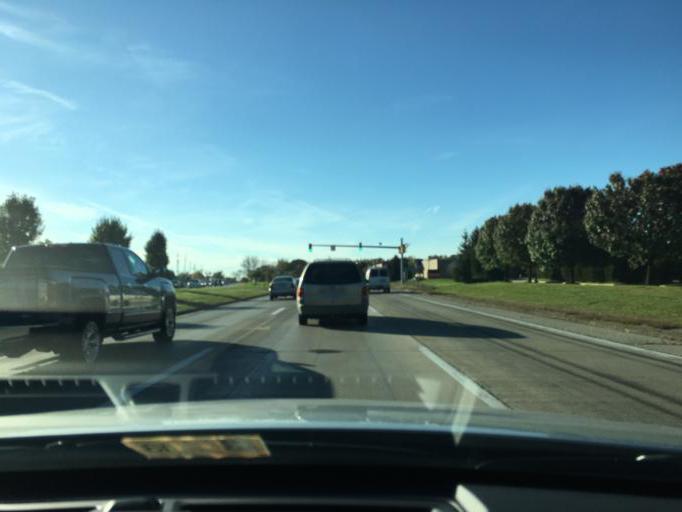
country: US
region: Michigan
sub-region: Macomb County
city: Fraser
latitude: 42.5673
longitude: -82.9842
